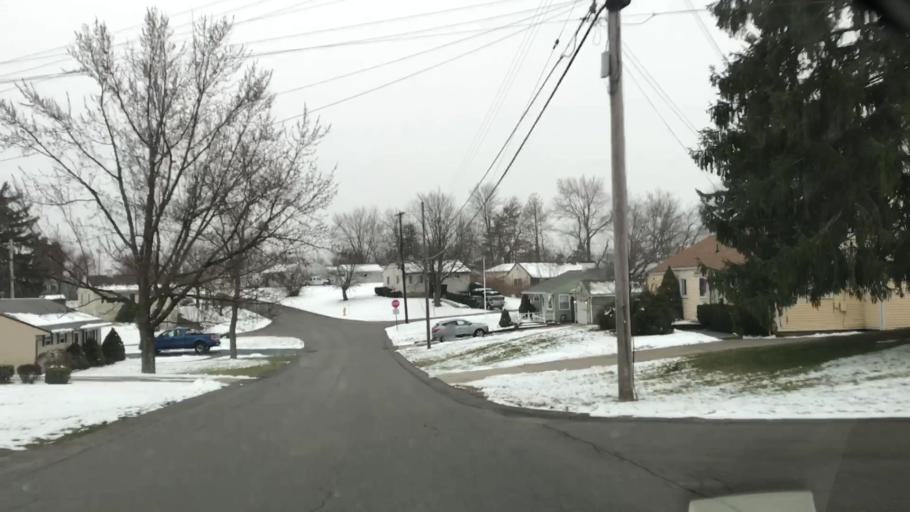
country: US
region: Pennsylvania
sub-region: Beaver County
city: Industry
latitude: 40.7033
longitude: -80.4019
